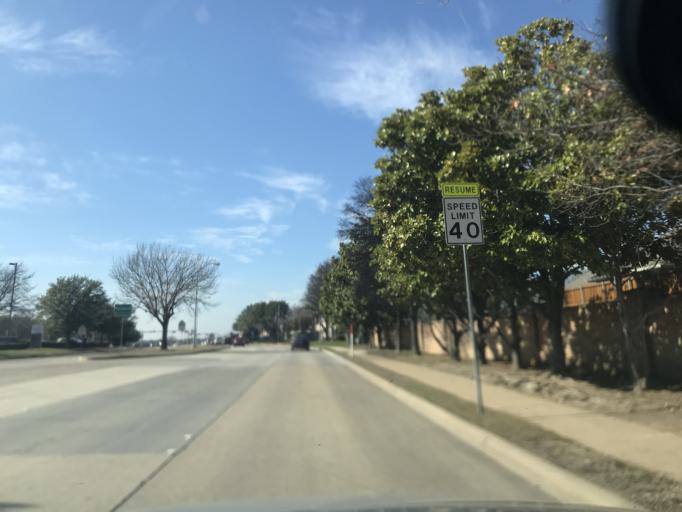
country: US
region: Texas
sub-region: Denton County
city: The Colony
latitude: 33.0453
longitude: -96.8240
